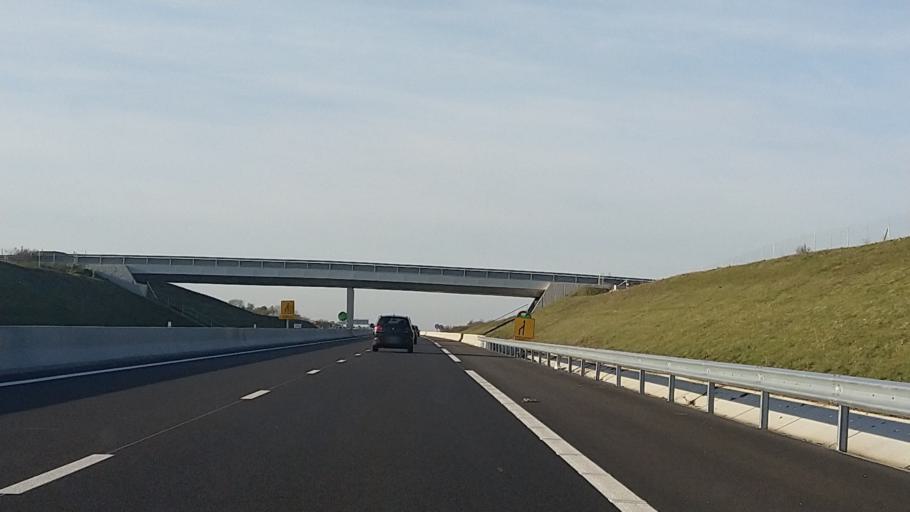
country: FR
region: Ile-de-France
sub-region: Departement du Val-d'Oise
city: Maffliers
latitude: 49.0852
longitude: 2.3196
